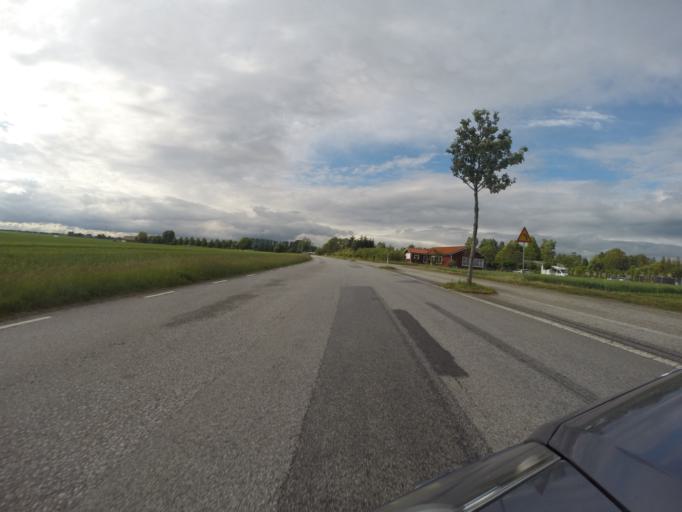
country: SE
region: Skane
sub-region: Kavlinge Kommun
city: Loddekopinge
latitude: 55.7729
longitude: 13.0110
